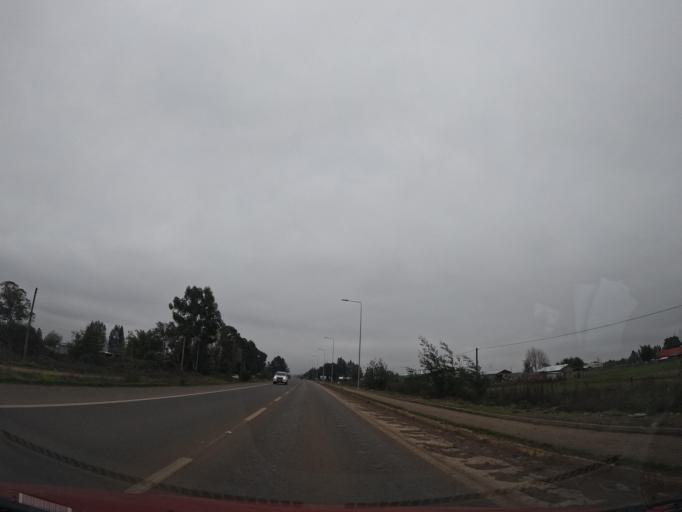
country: CL
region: Maule
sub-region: Provincia de Talca
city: San Clemente
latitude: -35.5221
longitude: -71.4886
